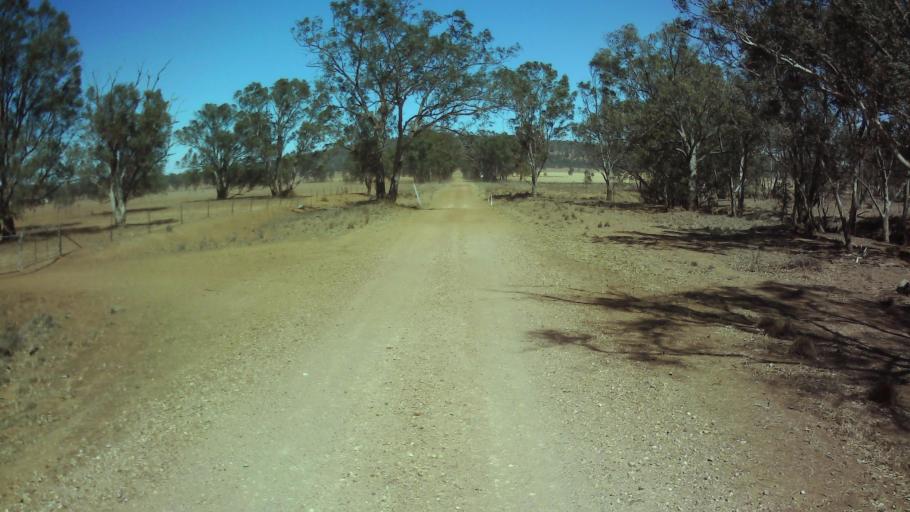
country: AU
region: New South Wales
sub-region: Weddin
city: Grenfell
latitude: -33.7052
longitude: 147.9798
